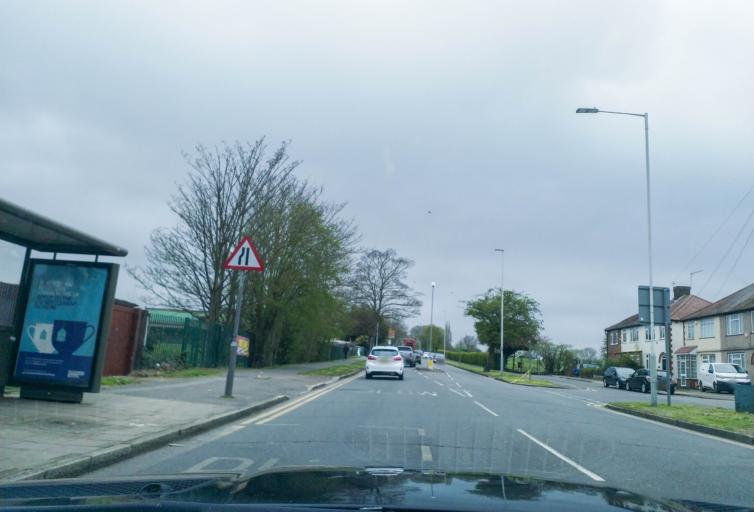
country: GB
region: England
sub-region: Greater London
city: Northolt
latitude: 51.5658
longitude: -0.3858
